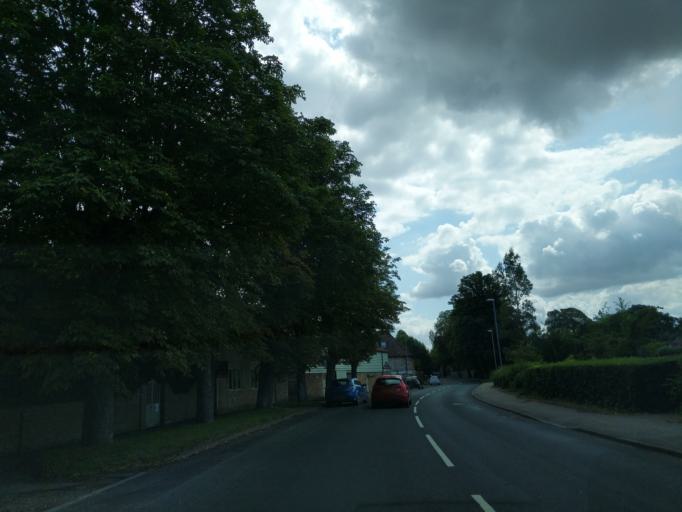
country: GB
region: England
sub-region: Cambridgeshire
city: Isleham
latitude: 52.3006
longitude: 0.4382
